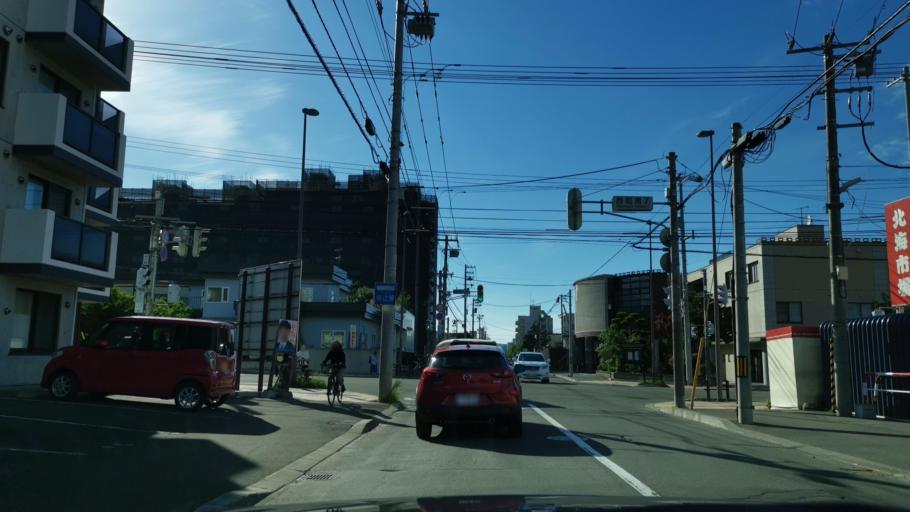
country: JP
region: Hokkaido
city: Sapporo
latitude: 43.0772
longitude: 141.2861
